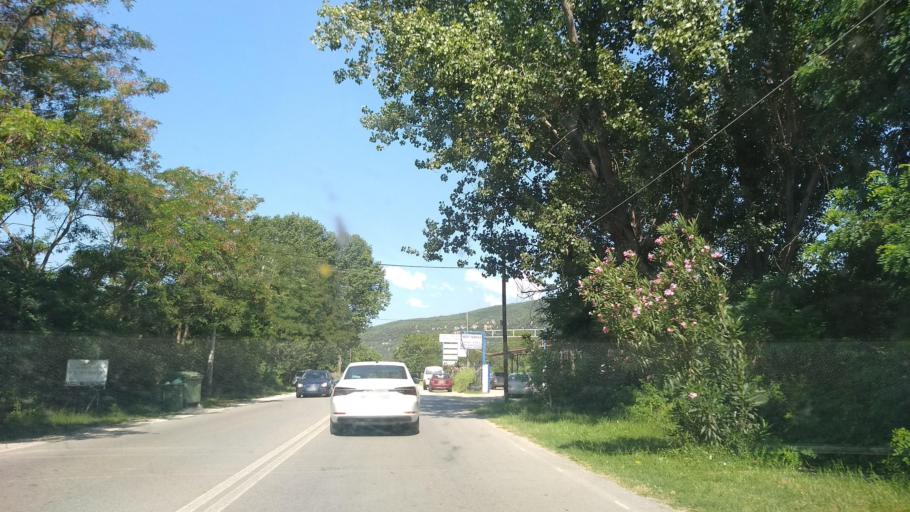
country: GR
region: Central Macedonia
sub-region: Nomos Thessalonikis
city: Stavros
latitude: 40.6681
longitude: 23.6801
